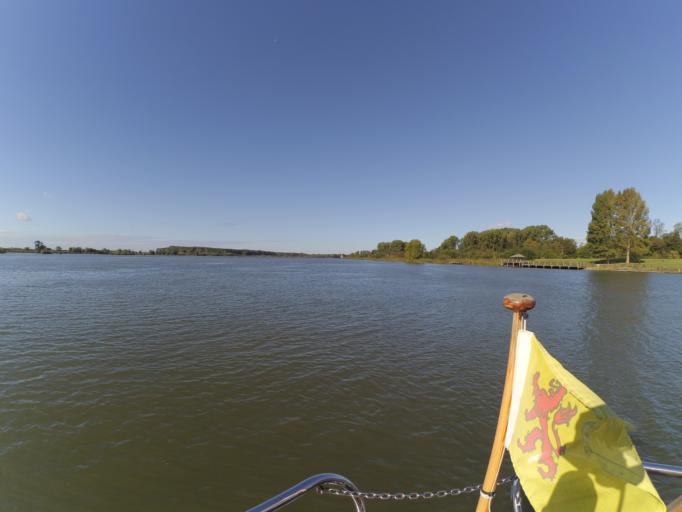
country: NL
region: South Holland
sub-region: Gemeente Barendrecht
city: Barendrecht
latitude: 51.8325
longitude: 4.5386
